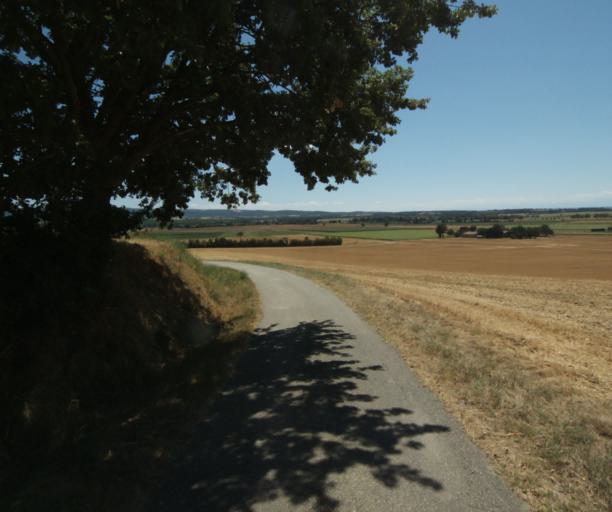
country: FR
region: Midi-Pyrenees
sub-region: Departement de la Haute-Garonne
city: Saint-Felix-Lauragais
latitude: 43.4597
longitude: 1.9230
